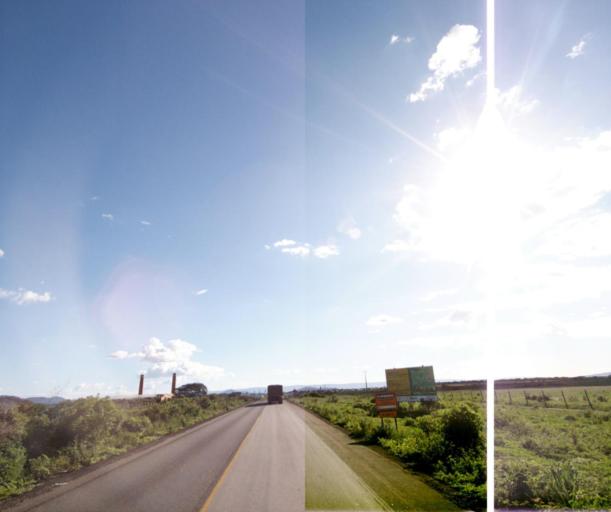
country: BR
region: Bahia
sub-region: Guanambi
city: Guanambi
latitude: -14.1805
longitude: -42.7342
